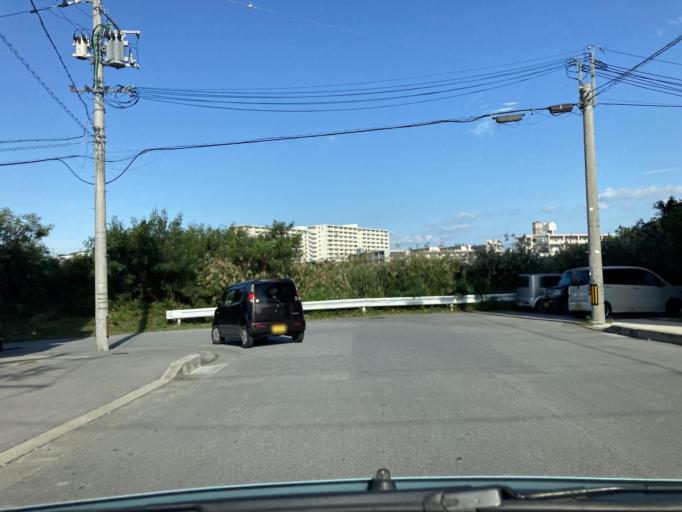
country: JP
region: Okinawa
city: Tomigusuku
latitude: 26.1927
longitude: 127.7153
